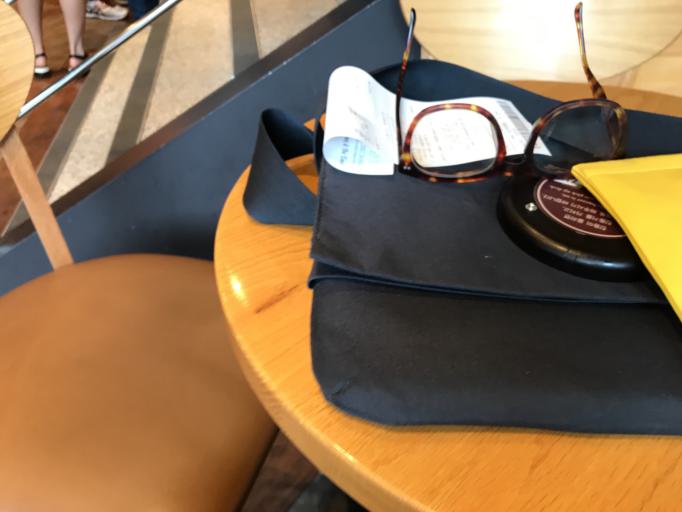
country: KR
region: Seoul
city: Seoul
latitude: 37.5760
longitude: 126.9853
